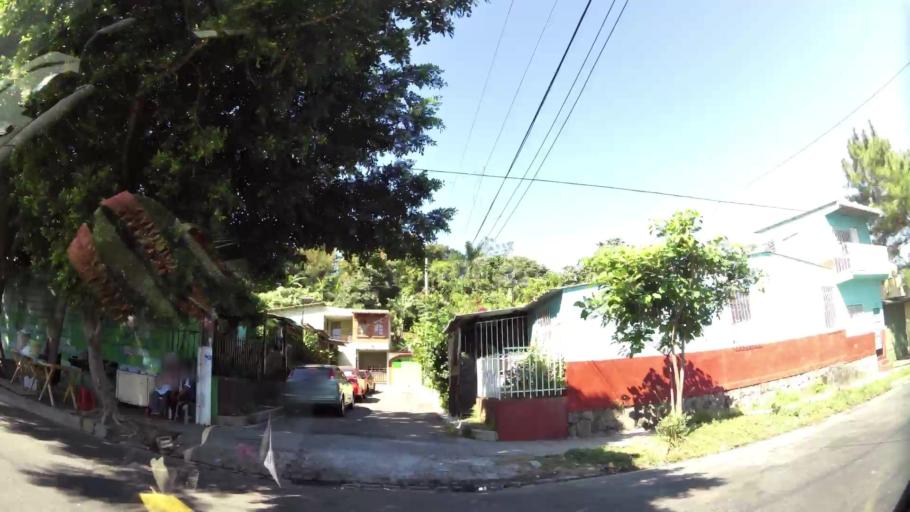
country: SV
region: La Libertad
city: Santa Tecla
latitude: 13.6682
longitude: -89.2894
